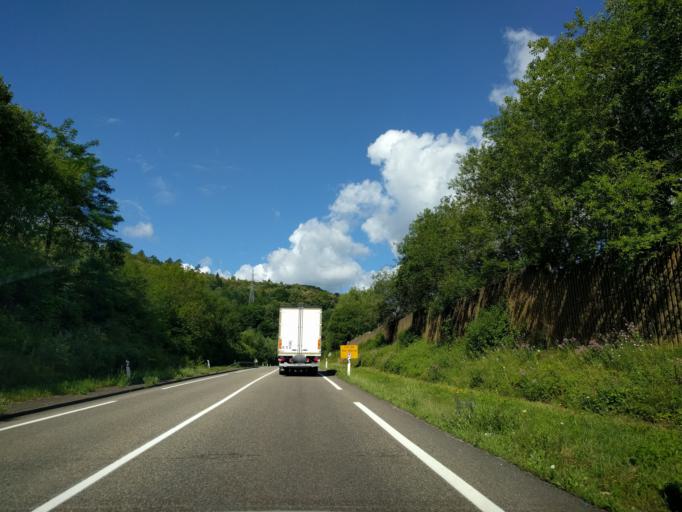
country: FR
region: Alsace
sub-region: Departement du Haut-Rhin
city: Liepvre
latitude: 48.2686
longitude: 7.2846
